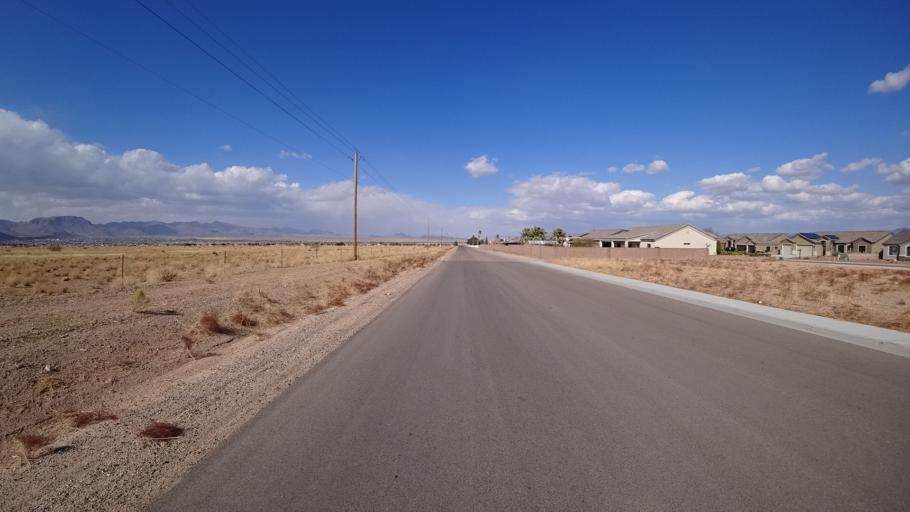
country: US
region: Arizona
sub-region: Mohave County
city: New Kingman-Butler
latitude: 35.2184
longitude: -113.9762
